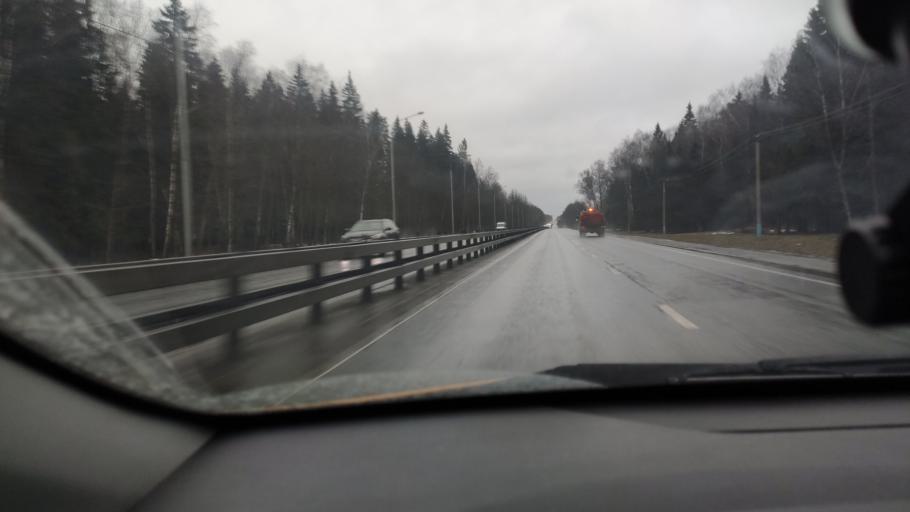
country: RU
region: Moskovskaya
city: Troitsk
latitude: 55.3453
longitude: 37.3208
